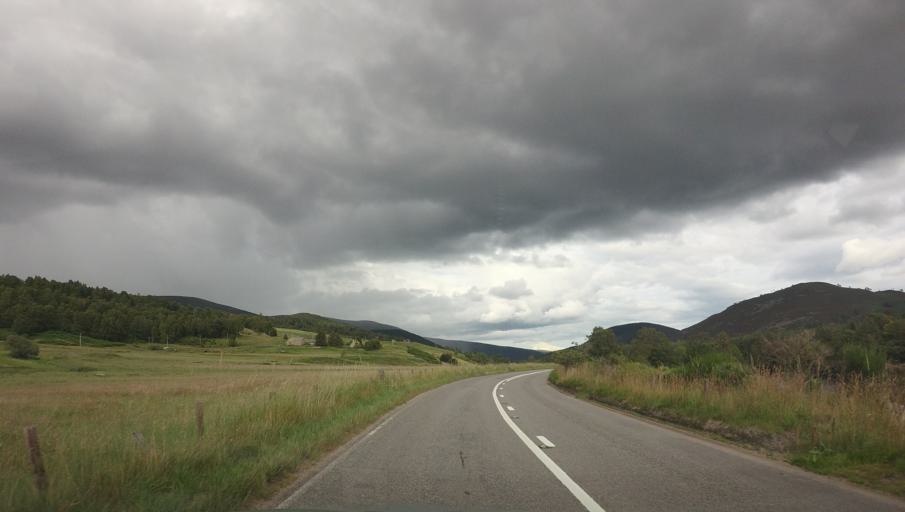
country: GB
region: Scotland
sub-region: Aberdeenshire
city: Ballater
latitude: 57.0418
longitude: -3.1919
